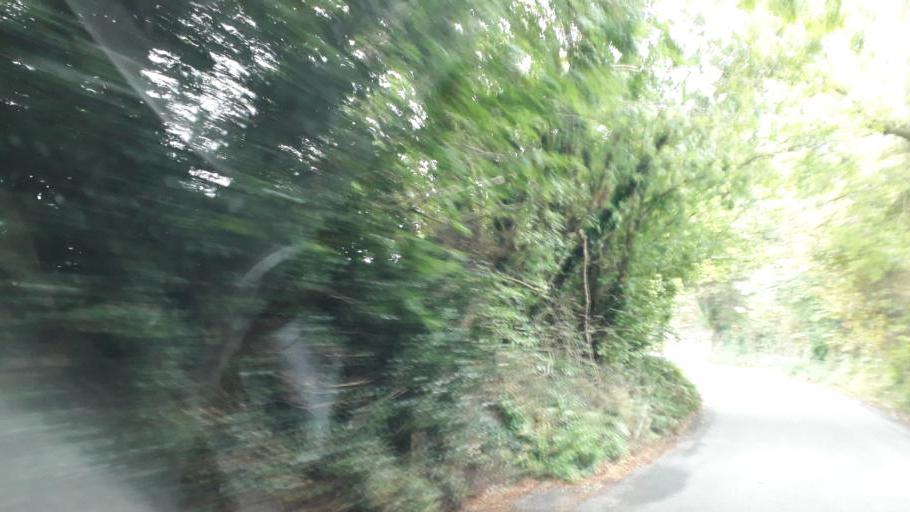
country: IE
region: Leinster
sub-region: Wicklow
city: Enniskerry
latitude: 53.1883
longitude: -6.2059
